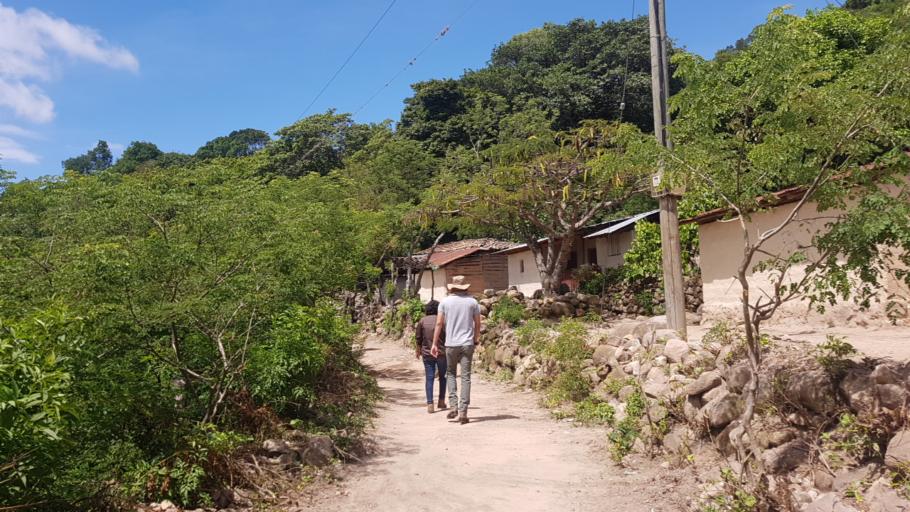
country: NI
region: Madriz
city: Somoto
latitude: 13.6046
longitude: -86.6130
